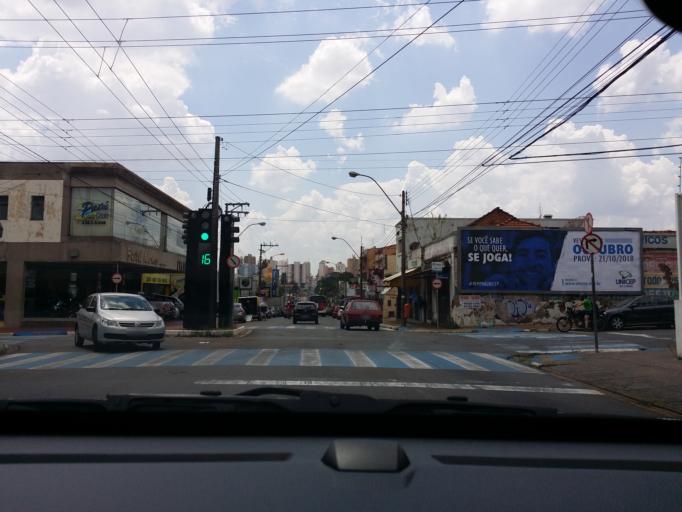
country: BR
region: Sao Paulo
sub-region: Sao Carlos
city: Sao Carlos
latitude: -22.0266
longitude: -47.8904
